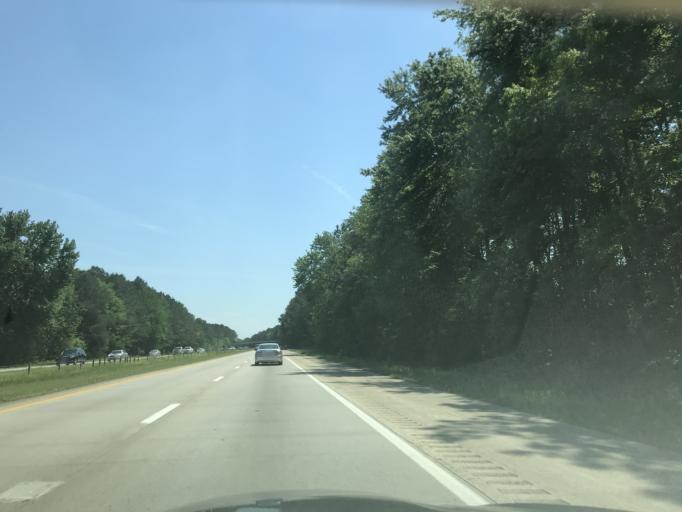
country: US
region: North Carolina
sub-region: Johnston County
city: Benson
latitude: 35.4776
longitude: -78.5503
